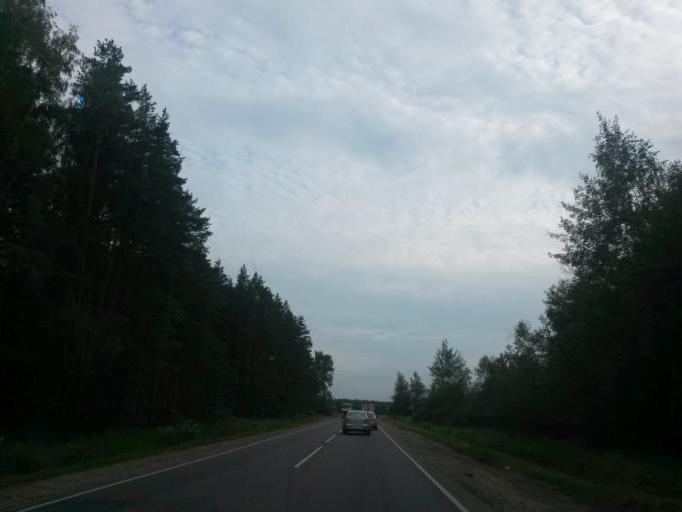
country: RU
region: Moskovskaya
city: Vostryakovo
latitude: 55.3634
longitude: 37.7752
